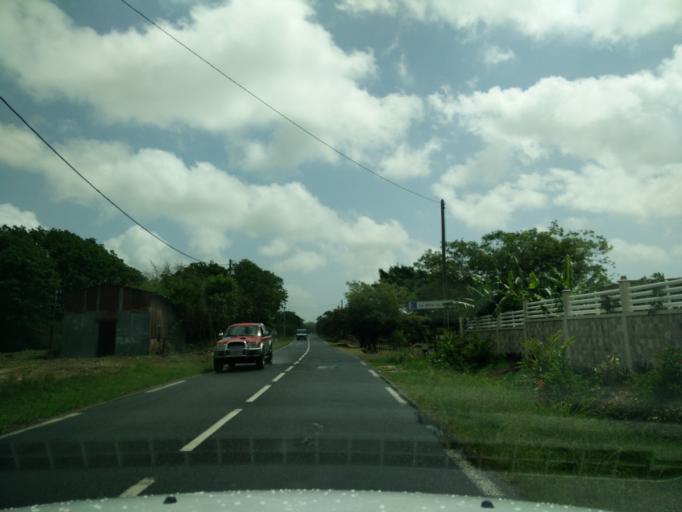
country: GP
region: Guadeloupe
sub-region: Guadeloupe
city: Grand-Bourg
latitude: 15.8994
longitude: -61.2868
